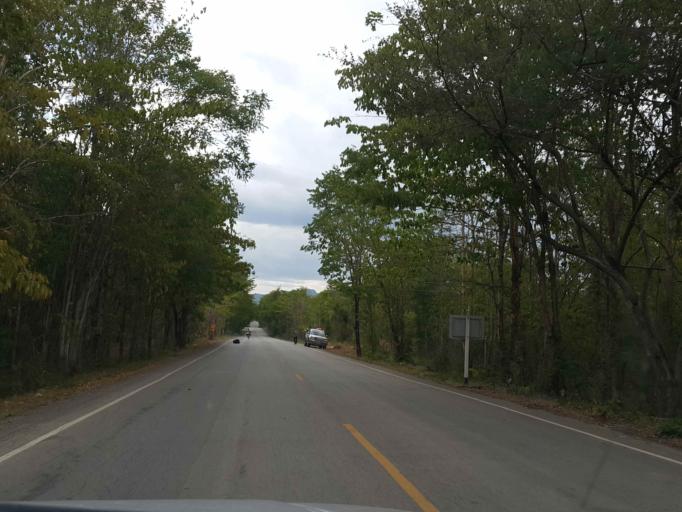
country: TH
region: Sukhothai
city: Thung Saliam
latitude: 17.3500
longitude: 99.4278
